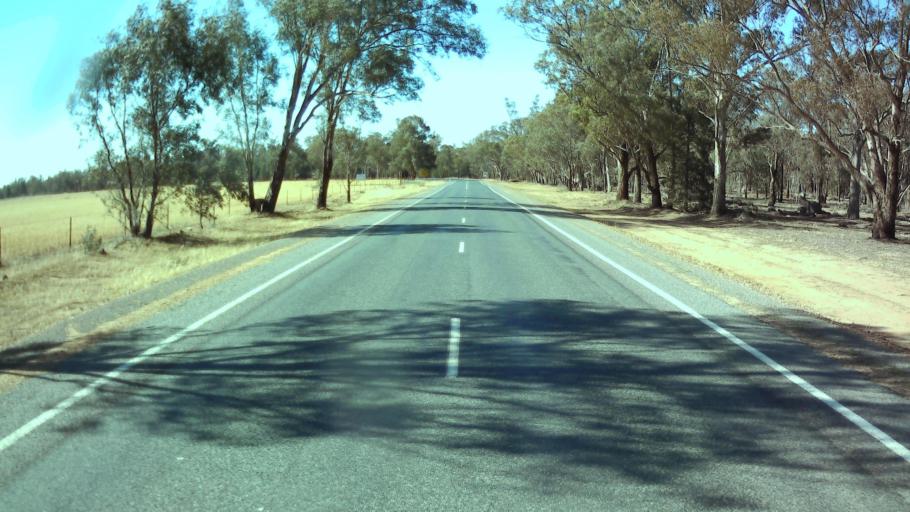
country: AU
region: New South Wales
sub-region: Weddin
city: Grenfell
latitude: -33.7323
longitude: 148.0888
